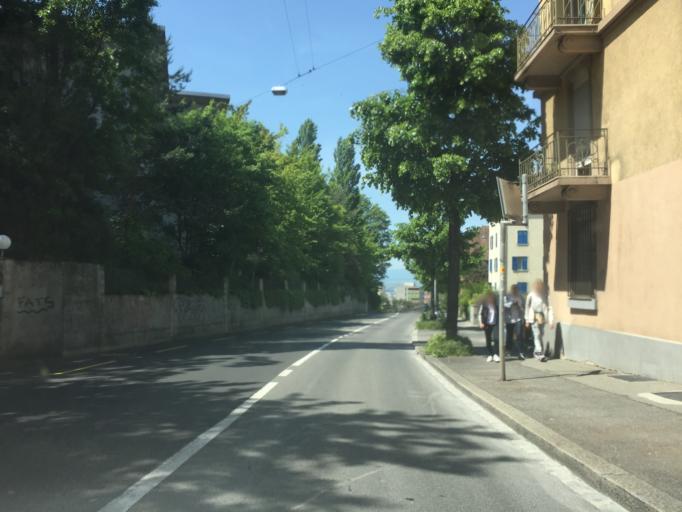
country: CH
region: Vaud
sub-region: Lausanne District
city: Lausanne
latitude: 46.5211
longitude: 6.6199
